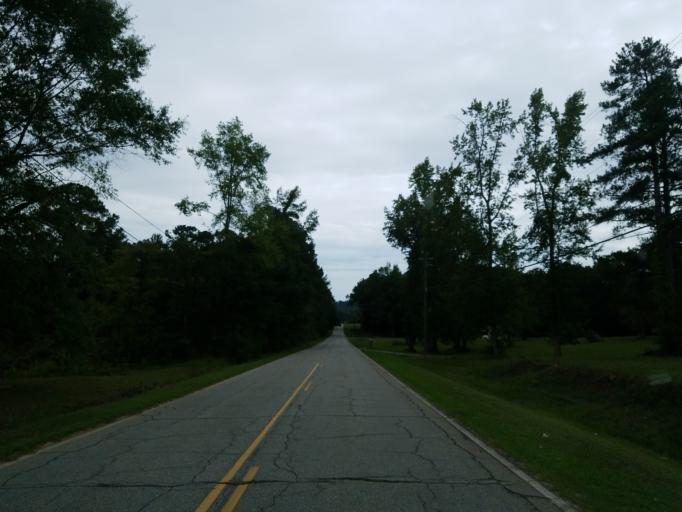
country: US
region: Georgia
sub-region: Lamar County
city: Barnesville
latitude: 33.0858
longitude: -84.1756
